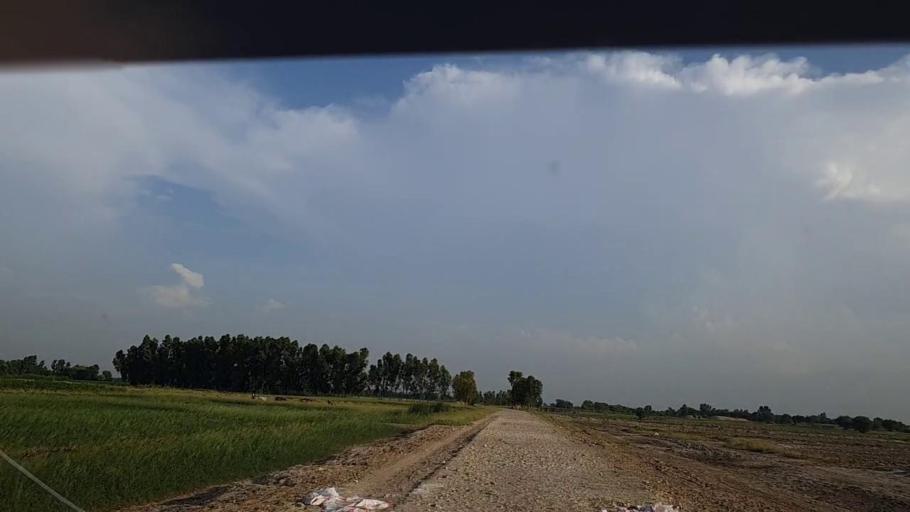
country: PK
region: Sindh
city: Khanpur
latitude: 27.8147
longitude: 69.3360
